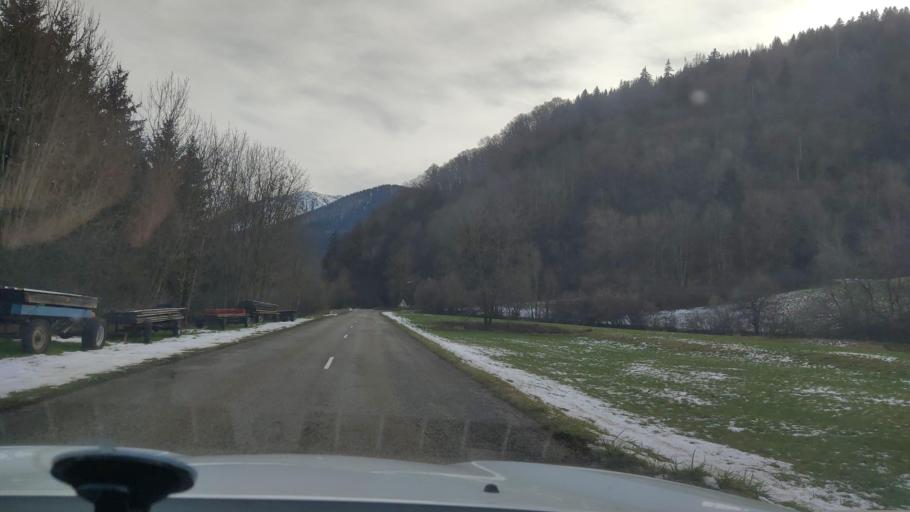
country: FR
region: Rhone-Alpes
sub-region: Departement de la Savoie
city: Gresy-sur-Isere
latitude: 45.6637
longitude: 6.1595
